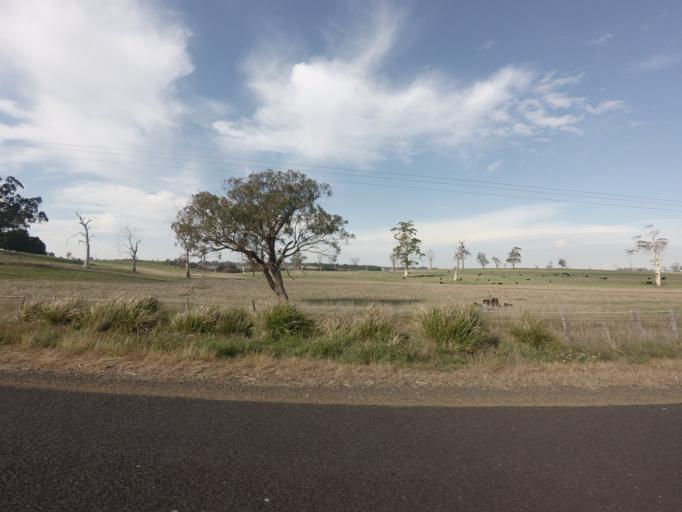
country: AU
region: Tasmania
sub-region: Northern Midlands
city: Longford
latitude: -41.5401
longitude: 146.9925
